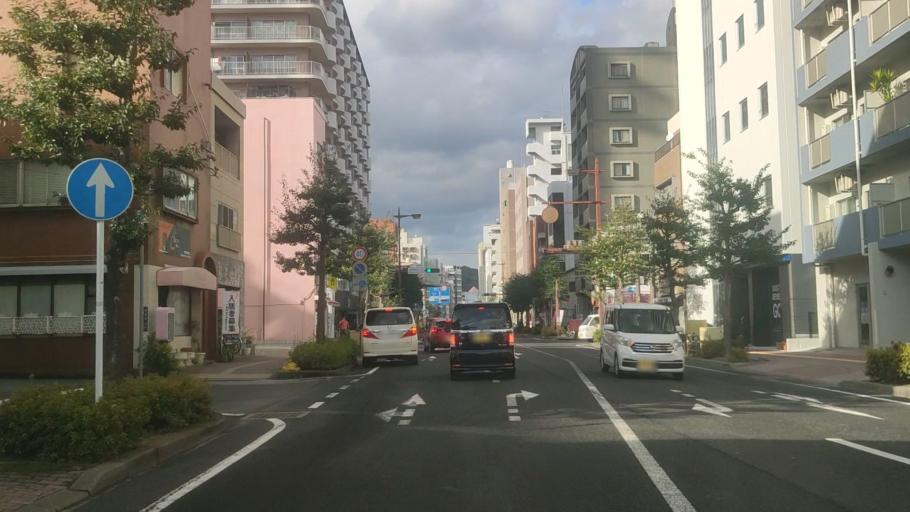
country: JP
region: Kagoshima
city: Kagoshima-shi
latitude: 31.5869
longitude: 130.5590
